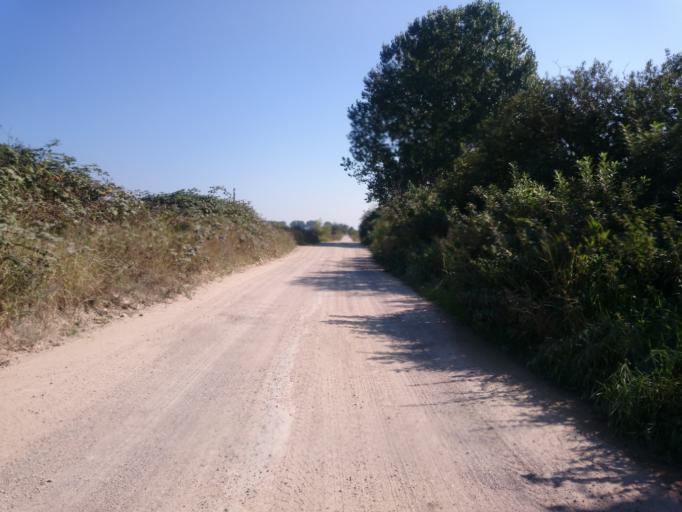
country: DE
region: Mecklenburg-Vorpommern
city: Barth
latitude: 54.3585
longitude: 12.6875
